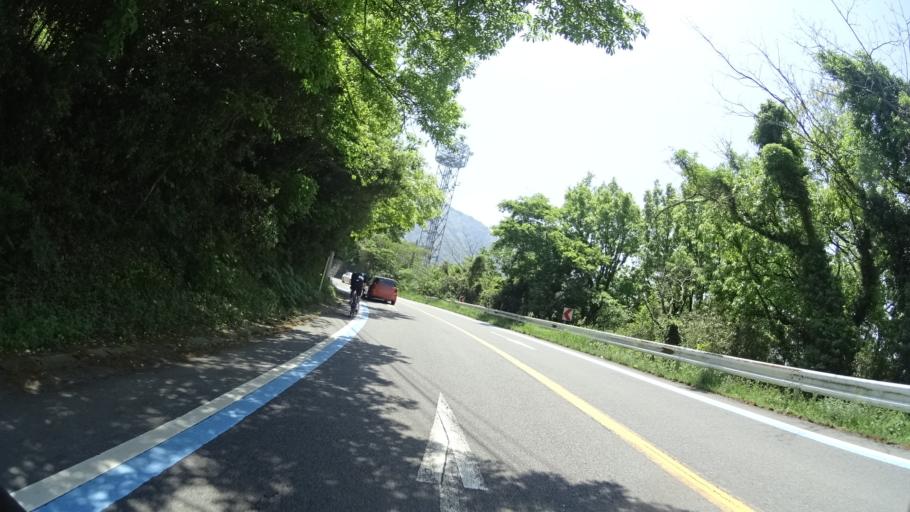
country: JP
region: Ehime
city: Iyo
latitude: 33.7124
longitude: 132.6681
